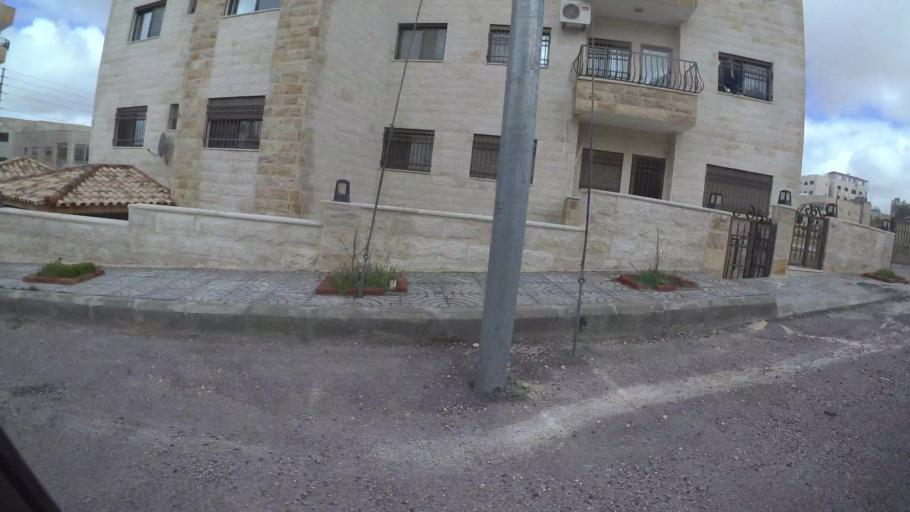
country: JO
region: Amman
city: Al Jubayhah
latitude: 32.0620
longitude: 35.8723
